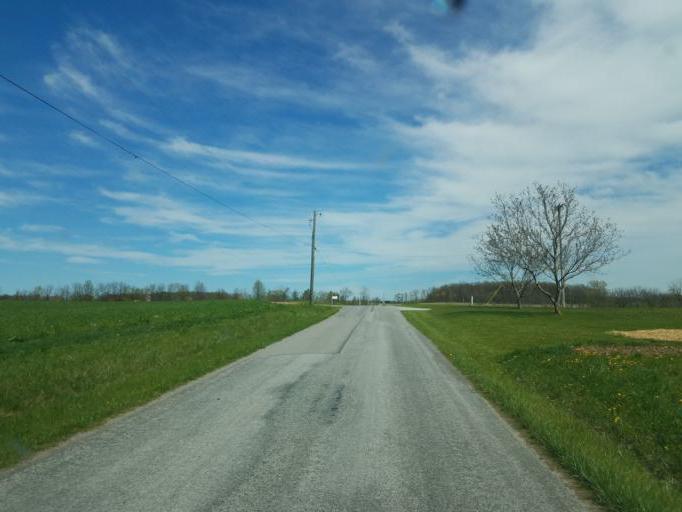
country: US
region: Ohio
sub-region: Huron County
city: Greenwich
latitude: 40.9020
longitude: -82.5064
